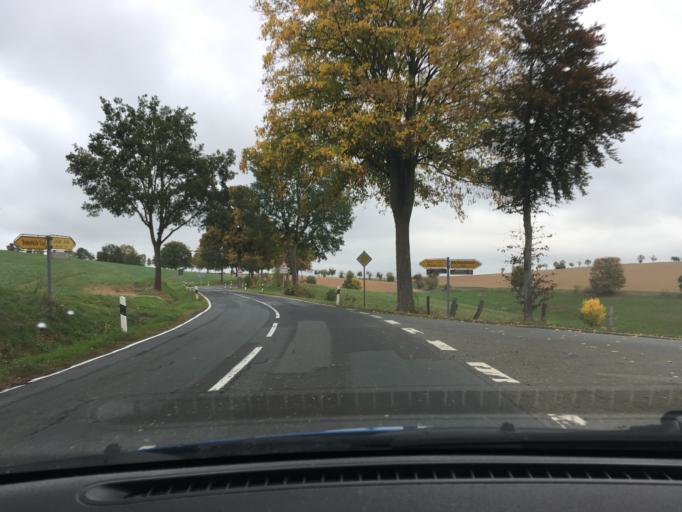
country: DE
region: Lower Saxony
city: Uslar
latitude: 51.6339
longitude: 9.6137
